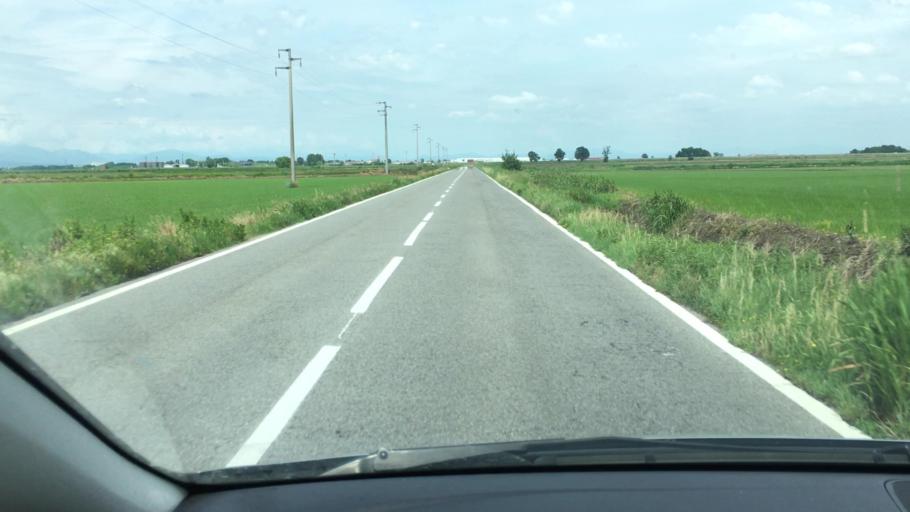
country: IT
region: Piedmont
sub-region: Provincia di Novara
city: Casalvolone
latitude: 45.4122
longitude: 8.4621
